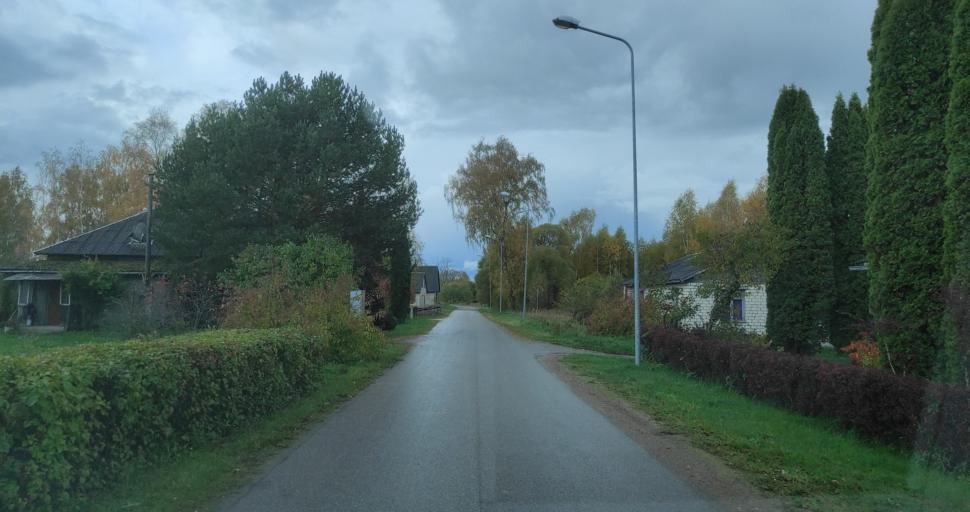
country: LV
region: Skrunda
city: Skrunda
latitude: 56.6859
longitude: 21.9986
